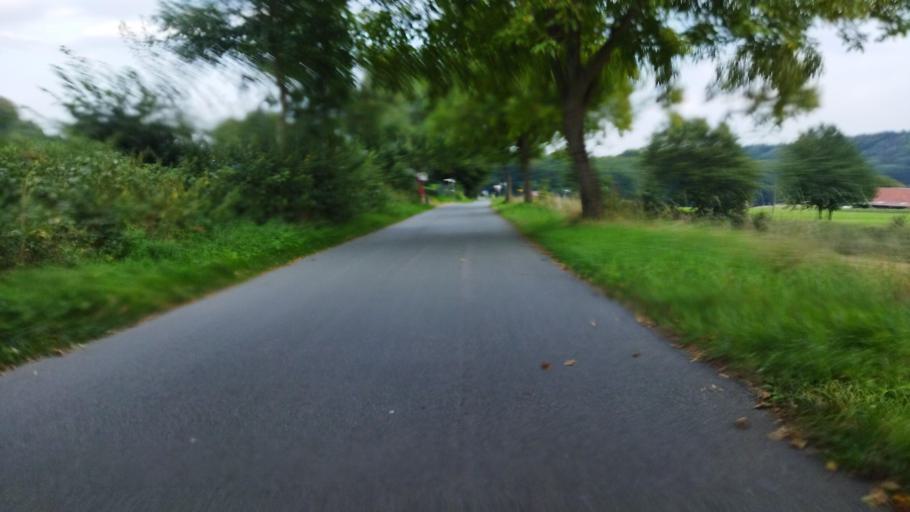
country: DE
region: Lower Saxony
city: Bad Iburg
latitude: 52.1676
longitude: 8.0260
